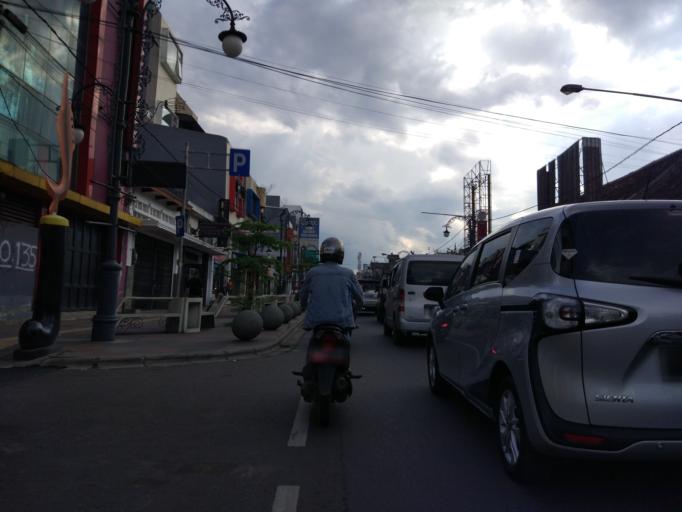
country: ID
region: West Java
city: Bandung
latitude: -6.9204
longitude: 107.5999
